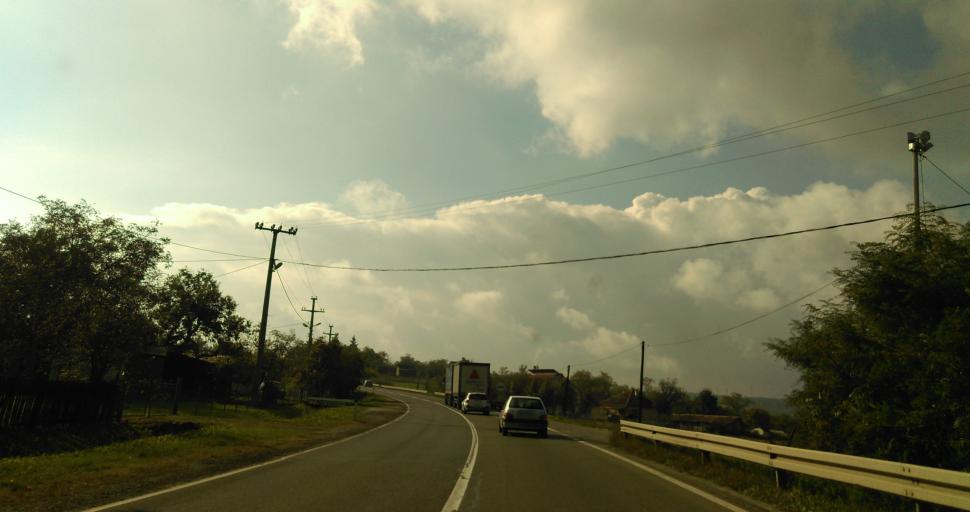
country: RS
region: Central Serbia
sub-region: Kolubarski Okrug
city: Lajkovac
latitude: 44.3584
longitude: 20.1897
